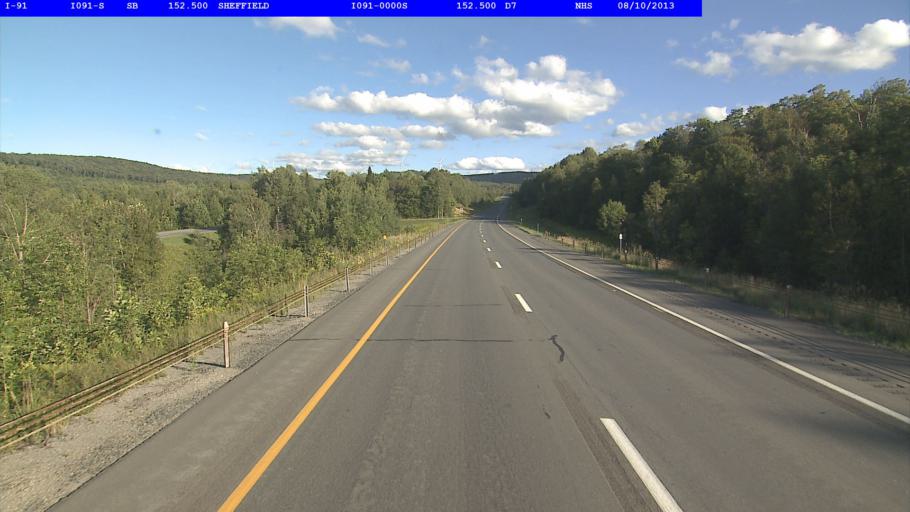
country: US
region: Vermont
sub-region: Caledonia County
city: Lyndonville
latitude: 44.6991
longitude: -72.1446
